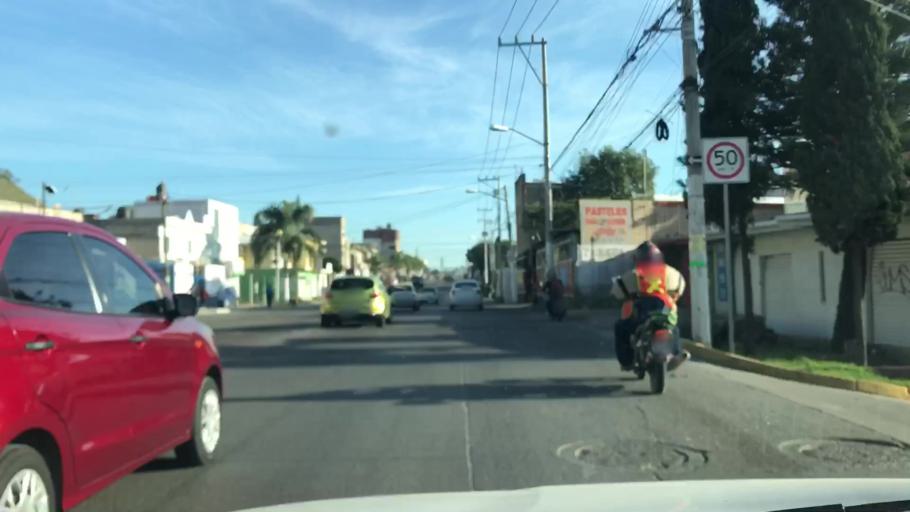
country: MX
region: Jalisco
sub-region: Tlajomulco de Zuniga
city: Palomar
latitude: 20.6509
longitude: -103.4558
